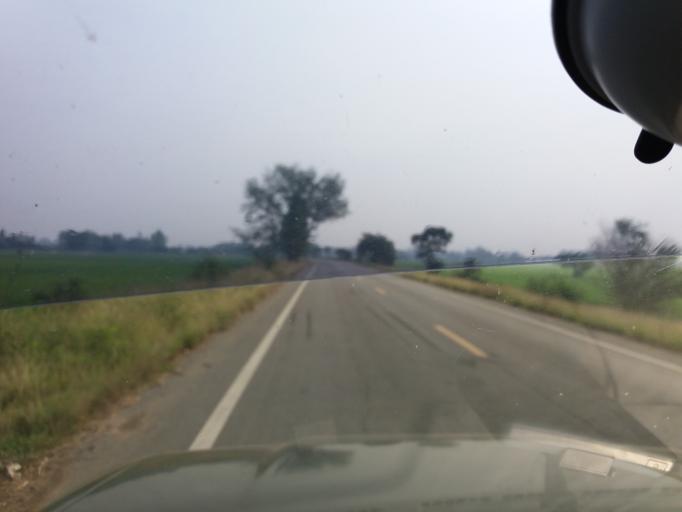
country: TH
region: Suphan Buri
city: Doem Bang Nang Buat
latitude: 14.8553
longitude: 100.1559
